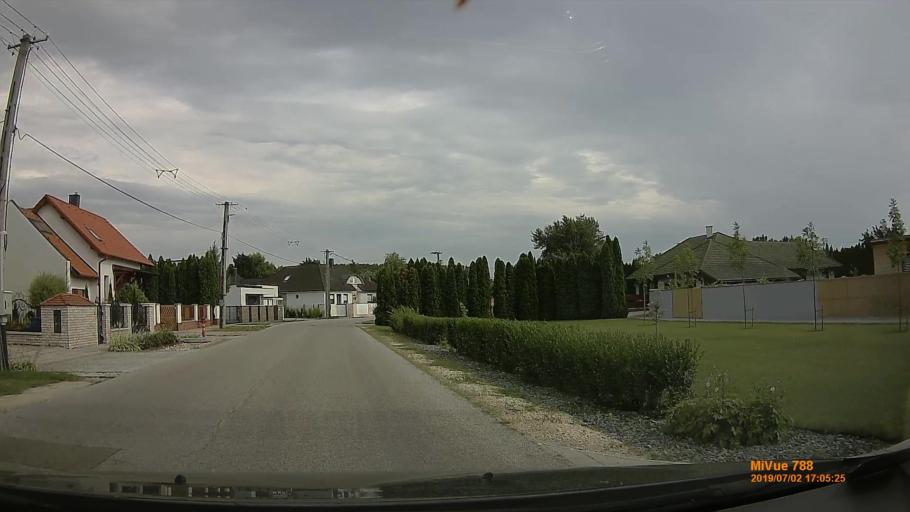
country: HU
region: Gyor-Moson-Sopron
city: Mosonmagyarovar
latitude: 47.8806
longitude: 17.2895
